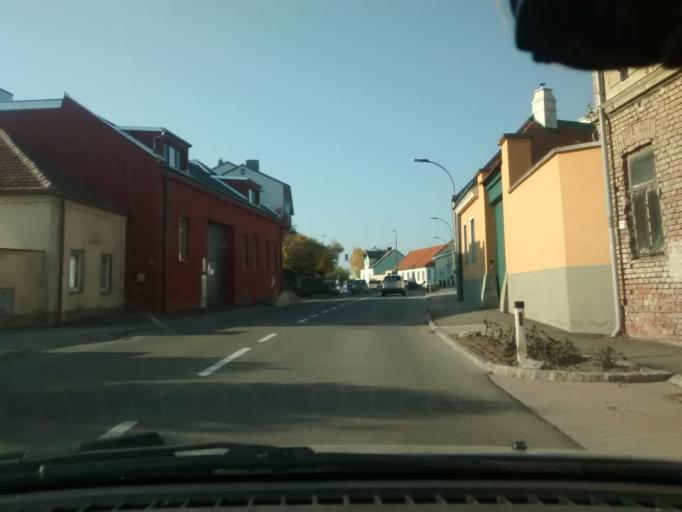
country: AT
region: Lower Austria
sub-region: Politischer Bezirk Modling
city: Achau
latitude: 48.0799
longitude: 16.3826
